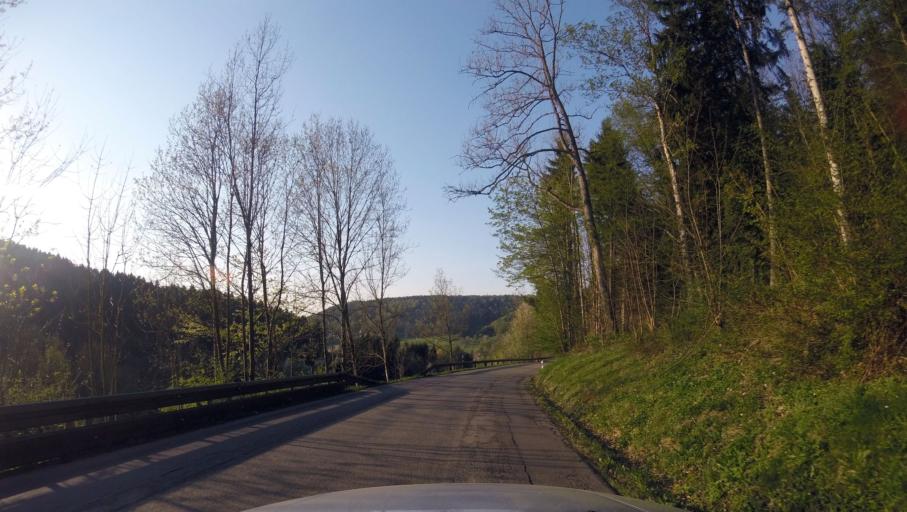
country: DE
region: Baden-Wuerttemberg
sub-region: Regierungsbezirk Stuttgart
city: Kaisersbach
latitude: 48.9545
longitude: 9.6616
